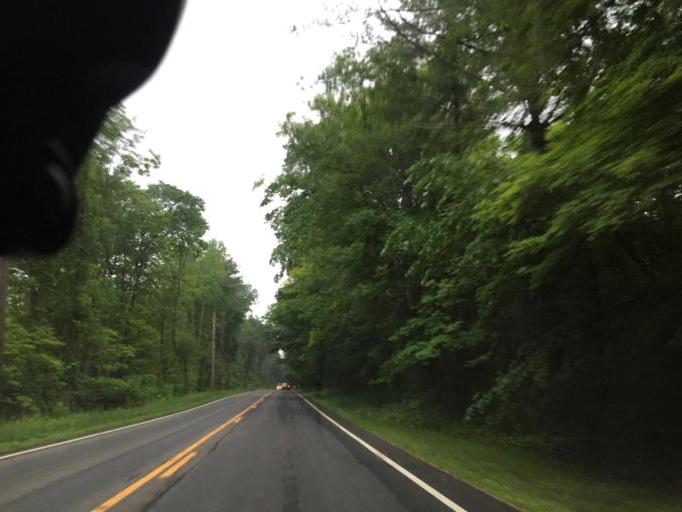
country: US
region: Connecticut
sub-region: Litchfield County
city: Canaan
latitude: 41.9445
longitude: -73.3127
